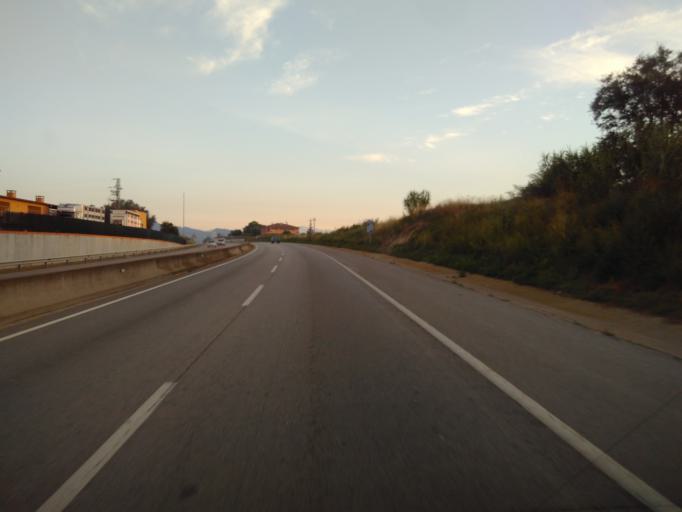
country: ES
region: Catalonia
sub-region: Provincia de Barcelona
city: Gurb
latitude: 41.9692
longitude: 2.2473
